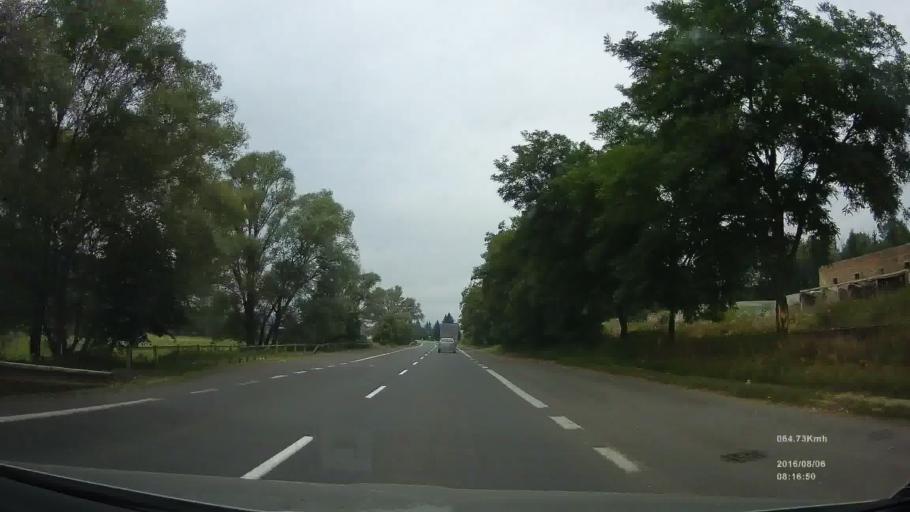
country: SK
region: Presovsky
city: Stropkov
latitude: 49.2148
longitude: 21.6418
